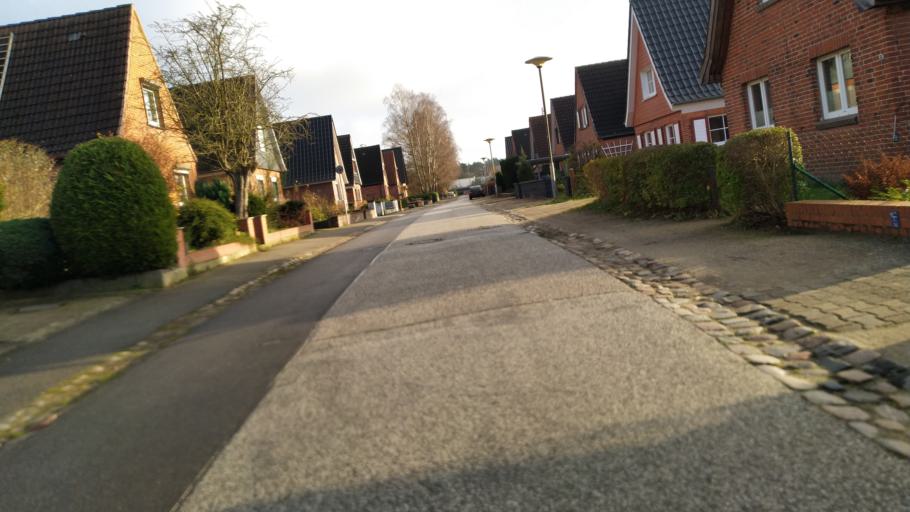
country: DE
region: Schleswig-Holstein
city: Ratekau
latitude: 53.9077
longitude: 10.7751
